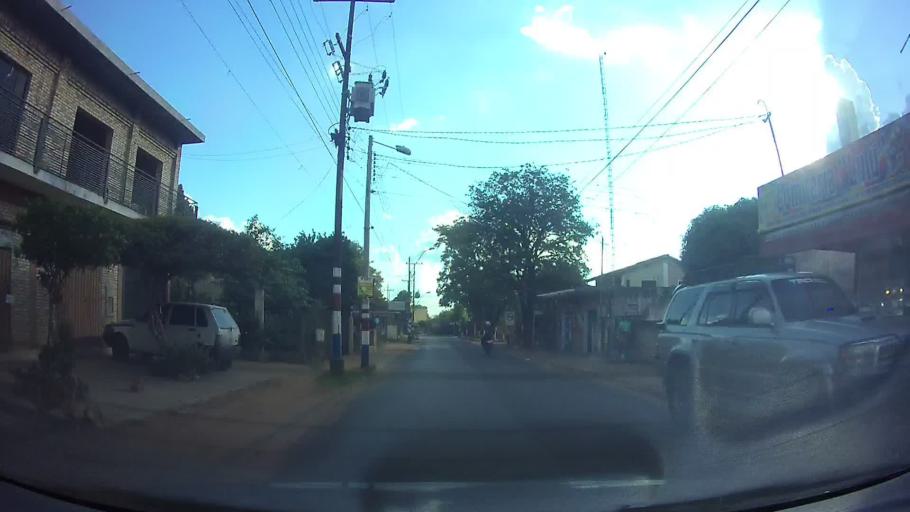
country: PY
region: Central
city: Aregua
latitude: -25.2909
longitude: -57.4409
